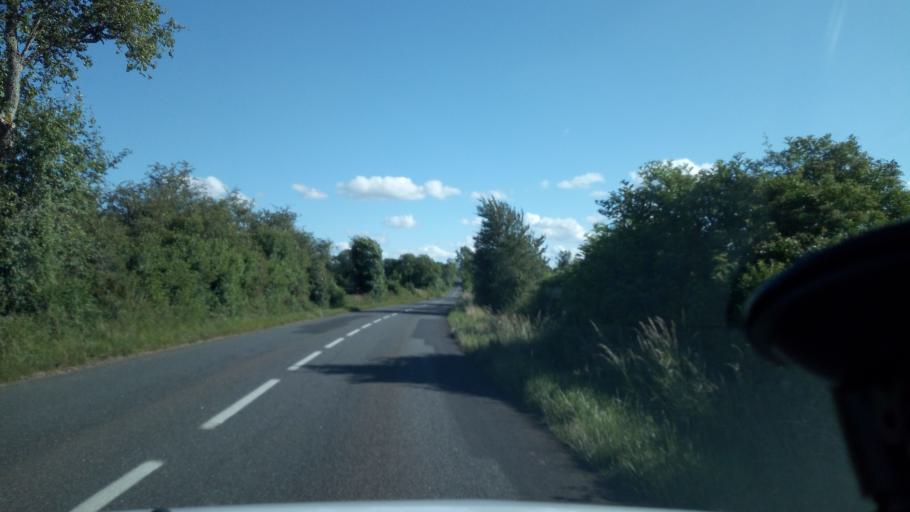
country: FR
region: Midi-Pyrenees
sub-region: Departement de l'Aveyron
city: Sebazac-Concoures
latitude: 44.4165
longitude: 2.6073
